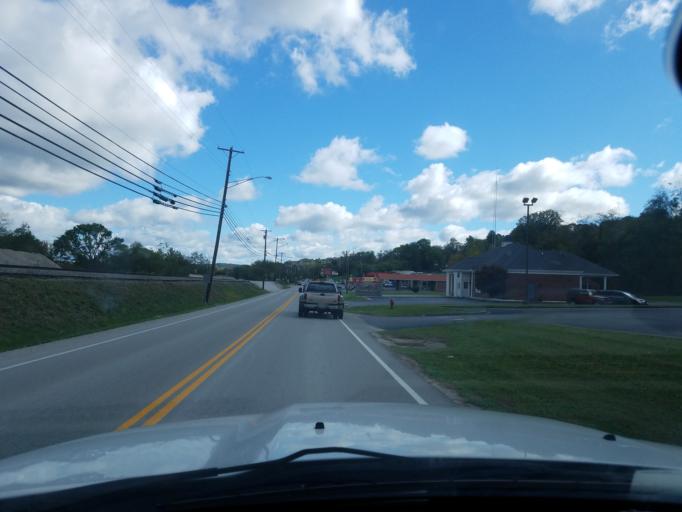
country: US
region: Kentucky
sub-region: Rockcastle County
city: Mount Vernon
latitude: 37.3512
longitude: -84.3486
